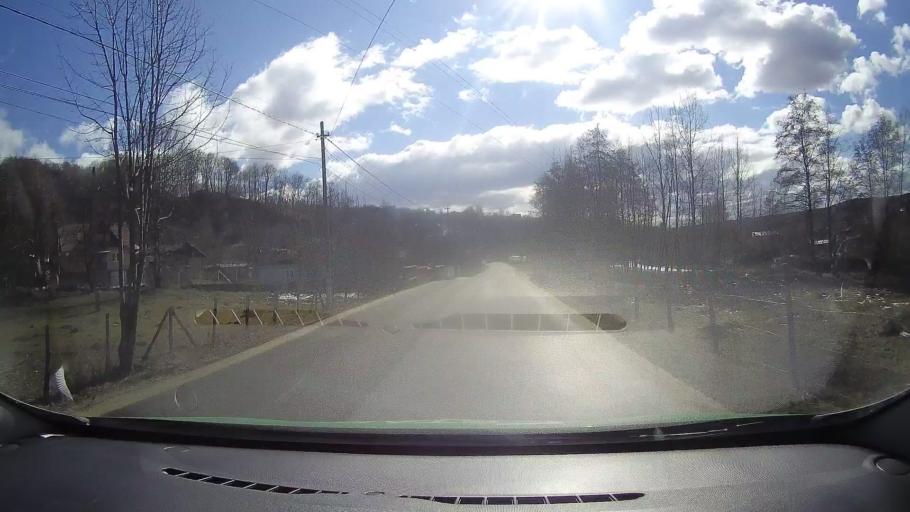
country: RO
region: Dambovita
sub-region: Comuna Runcu
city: Badeni
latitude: 45.1503
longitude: 25.4020
